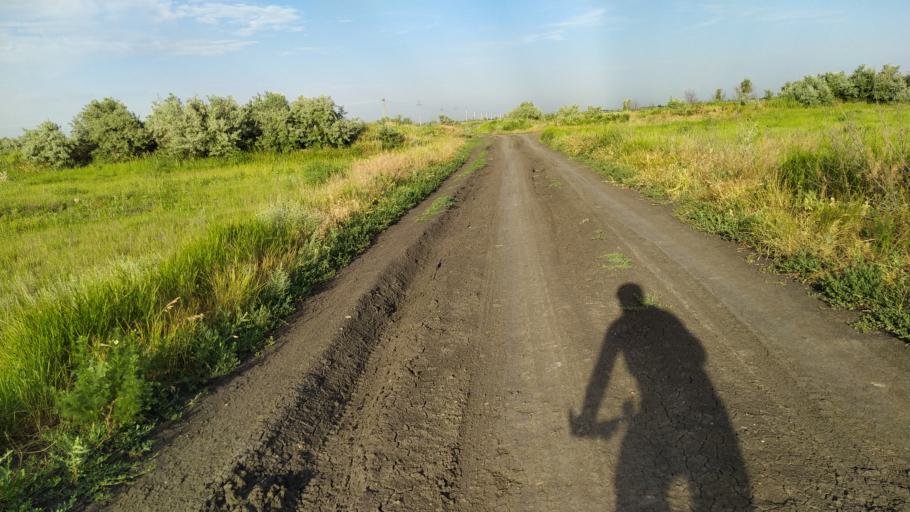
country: RU
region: Rostov
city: Kuleshovka
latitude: 47.1382
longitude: 39.6418
